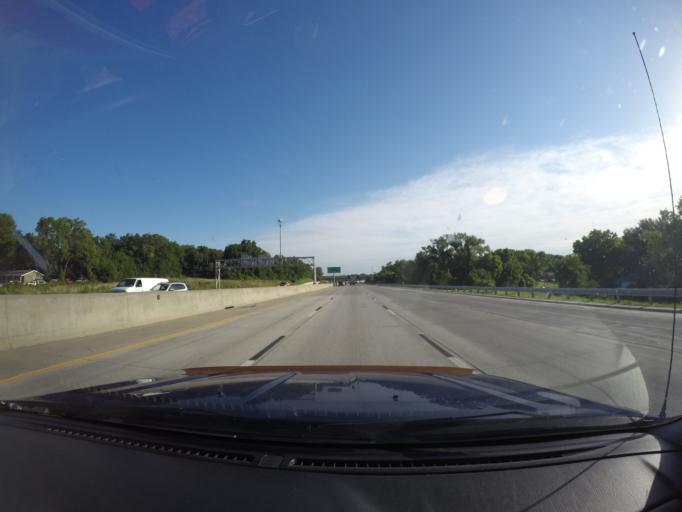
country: US
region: Kansas
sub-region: Wyandotte County
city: Kansas City
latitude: 39.1326
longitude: -94.6763
